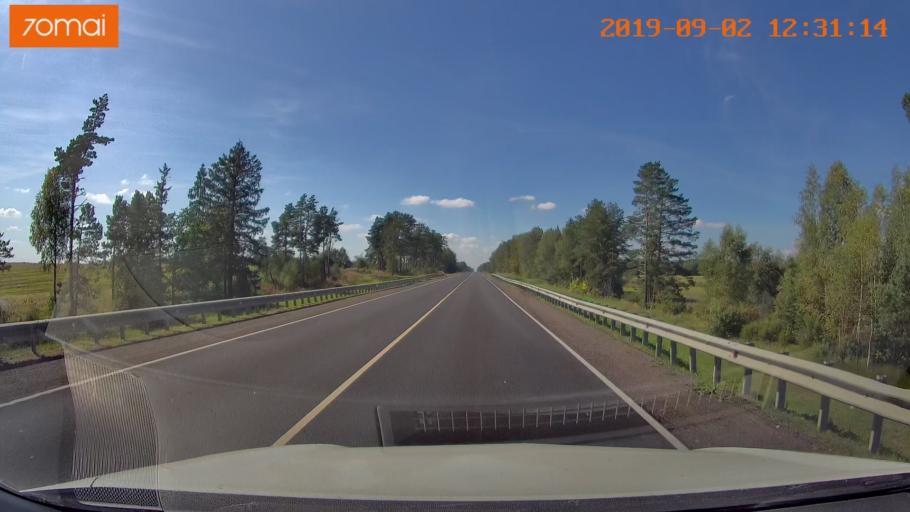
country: RU
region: Smolensk
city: Shumyachi
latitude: 53.8261
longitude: 32.4551
